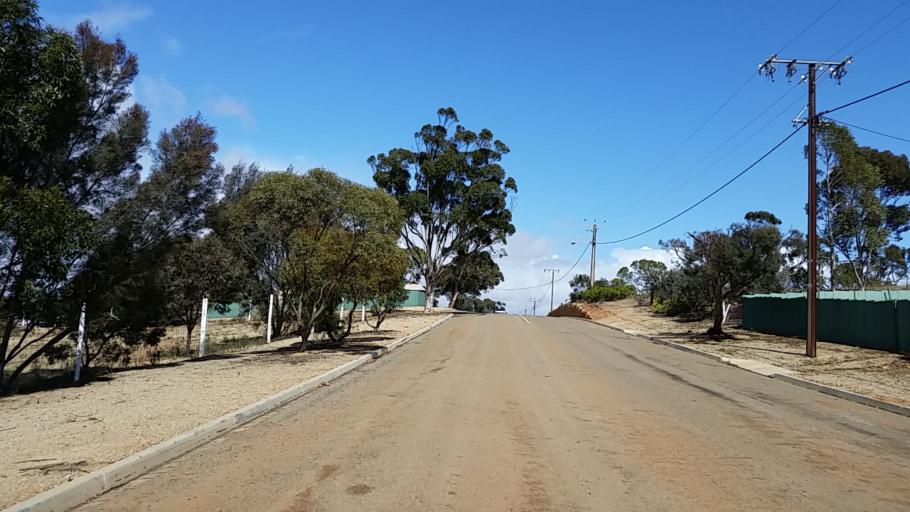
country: AU
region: South Australia
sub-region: Peterborough
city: Peterborough
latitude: -32.9703
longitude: 138.8353
